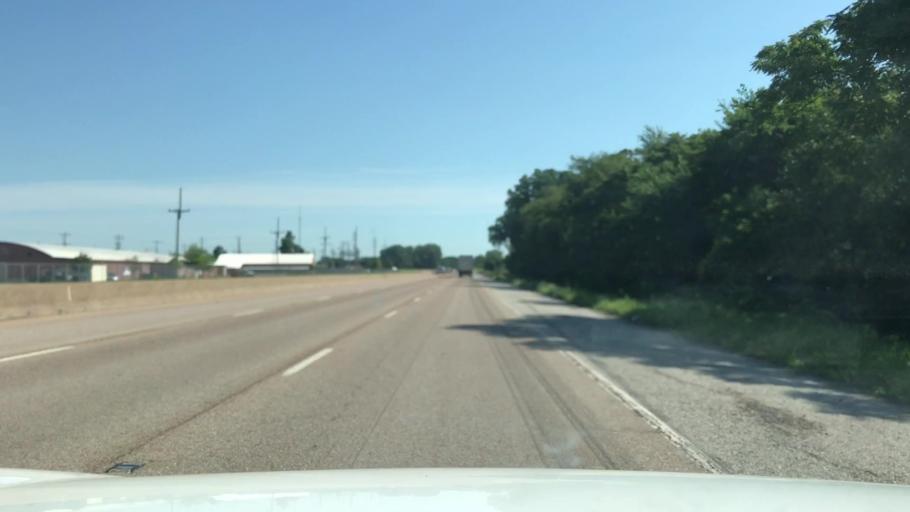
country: US
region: Illinois
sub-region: Madison County
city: Madison
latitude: 38.6880
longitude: -90.1709
